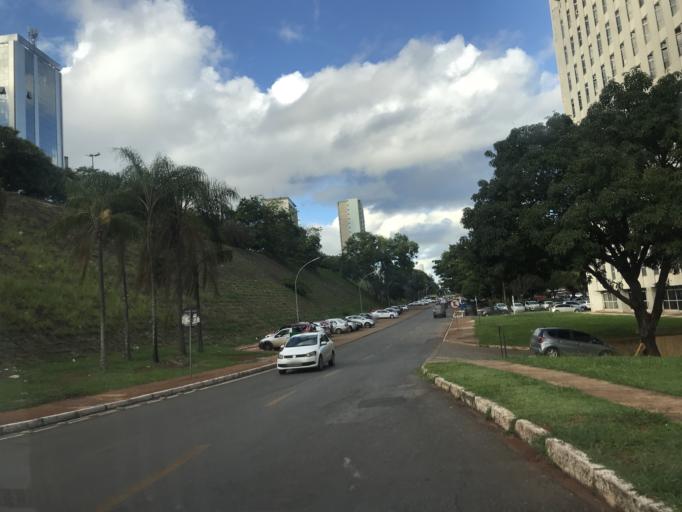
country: BR
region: Federal District
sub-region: Brasilia
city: Brasilia
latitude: -15.8021
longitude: -47.8817
